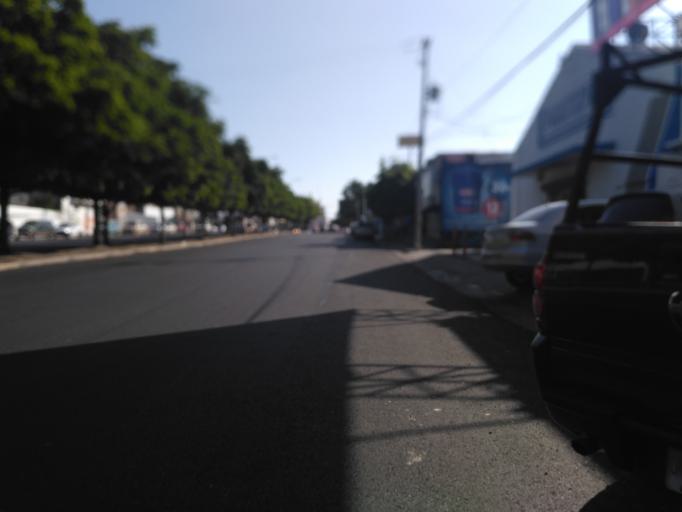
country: MX
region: Sinaloa
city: Culiacan
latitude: 24.7959
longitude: -107.4038
